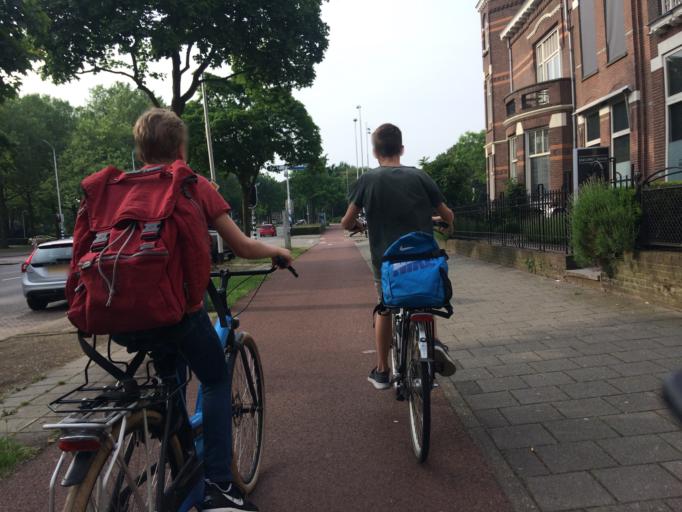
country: NL
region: Gelderland
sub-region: Gemeente Nijmegen
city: Nijmegen
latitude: 51.8420
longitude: 5.8662
